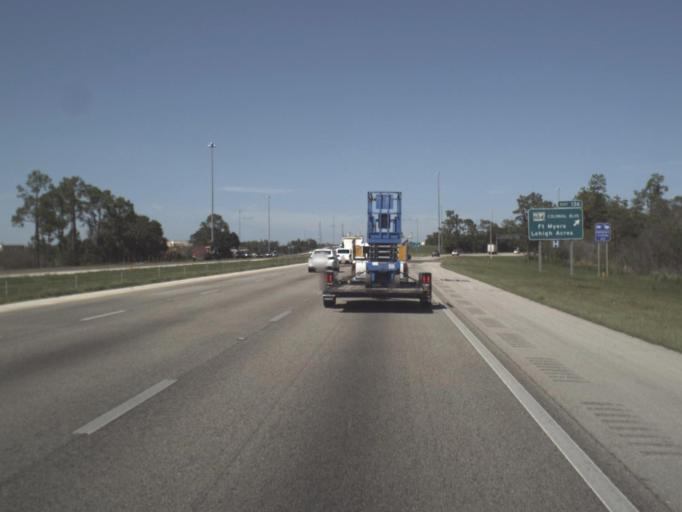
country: US
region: Florida
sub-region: Lee County
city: Fort Myers
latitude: 26.6059
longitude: -81.8010
